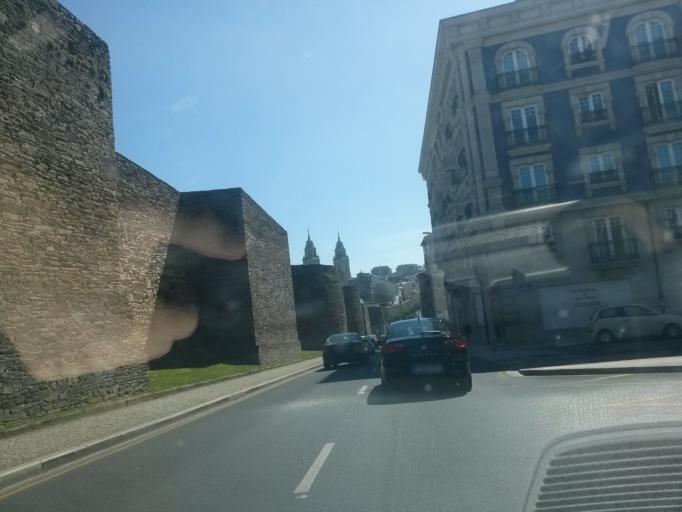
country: ES
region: Galicia
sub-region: Provincia de Lugo
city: Lugo
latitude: 43.0111
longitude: -7.5624
